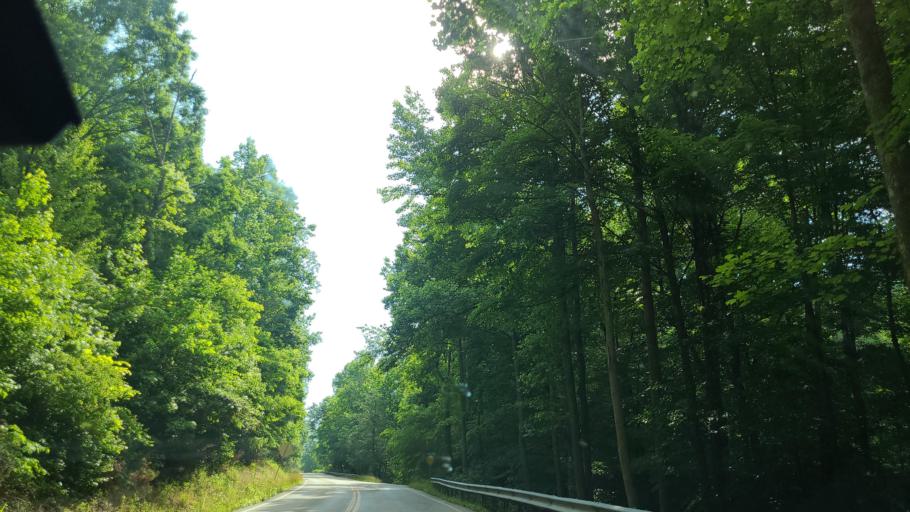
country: US
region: Kentucky
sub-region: Knox County
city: Barbourville
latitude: 36.6863
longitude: -83.8815
